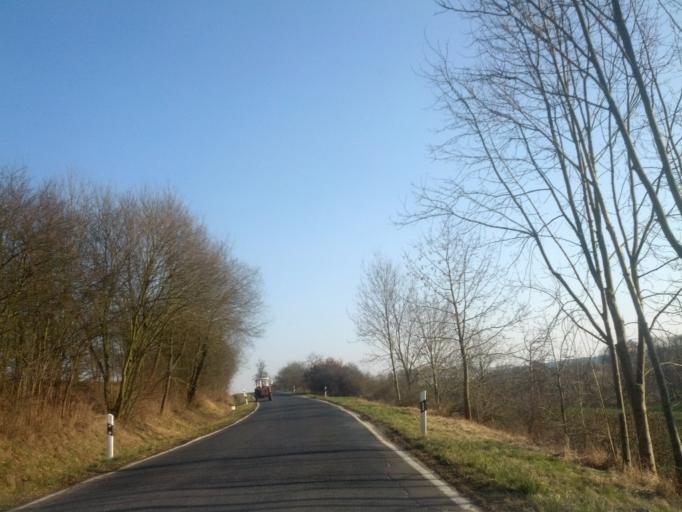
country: DE
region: Thuringia
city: Lauterbach
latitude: 51.0643
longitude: 10.3555
